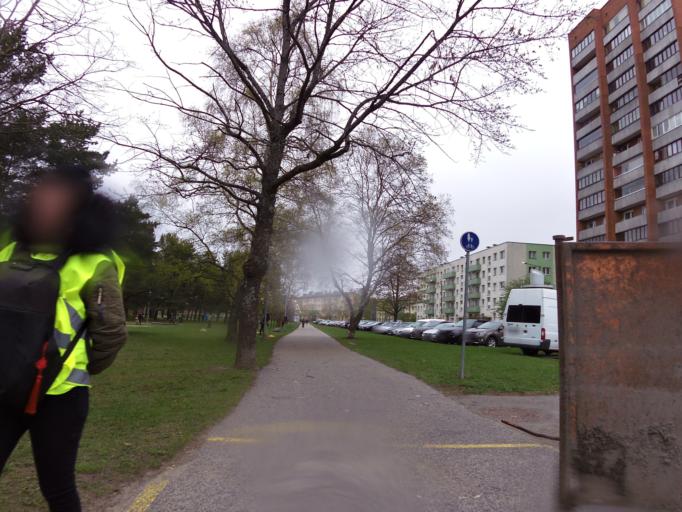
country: EE
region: Harju
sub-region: Tallinna linn
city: Tallinn
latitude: 59.4423
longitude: 24.6862
